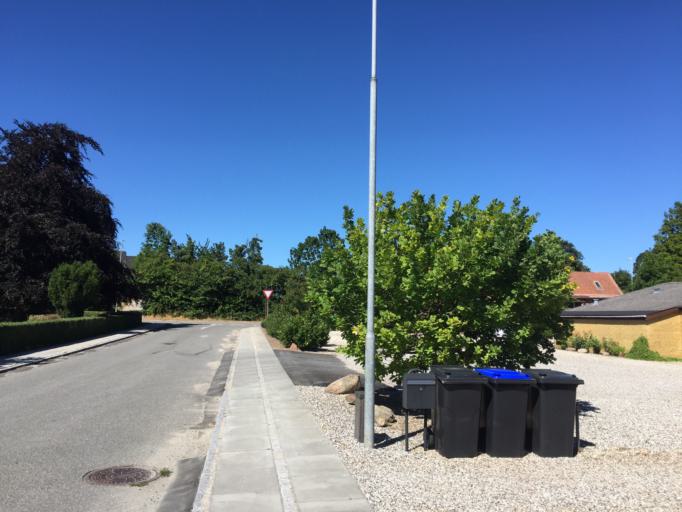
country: DK
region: South Denmark
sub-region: Nordfyns Kommune
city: Sonderso
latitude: 55.5338
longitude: 10.3071
